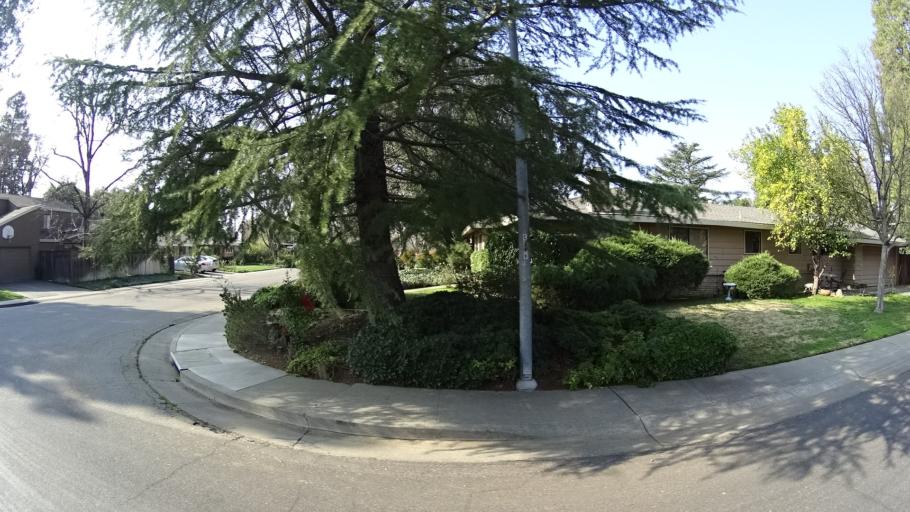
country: US
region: California
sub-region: Yolo County
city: Davis
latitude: 38.5498
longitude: -121.7748
